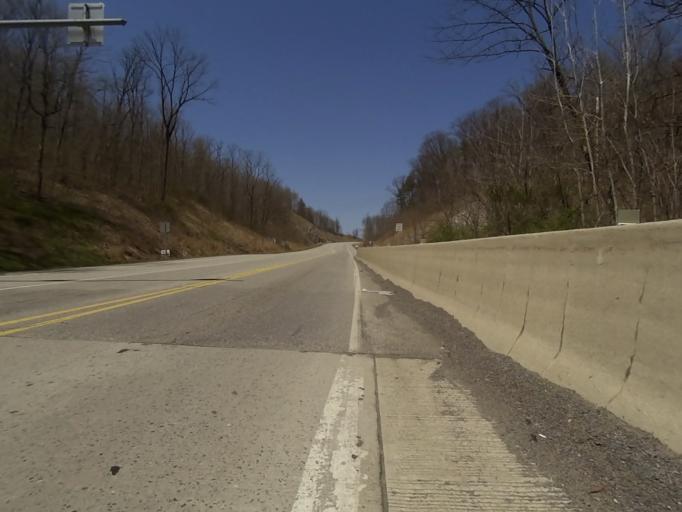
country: US
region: Pennsylvania
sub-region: Blair County
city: Williamsburg
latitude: 40.5720
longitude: -78.1390
